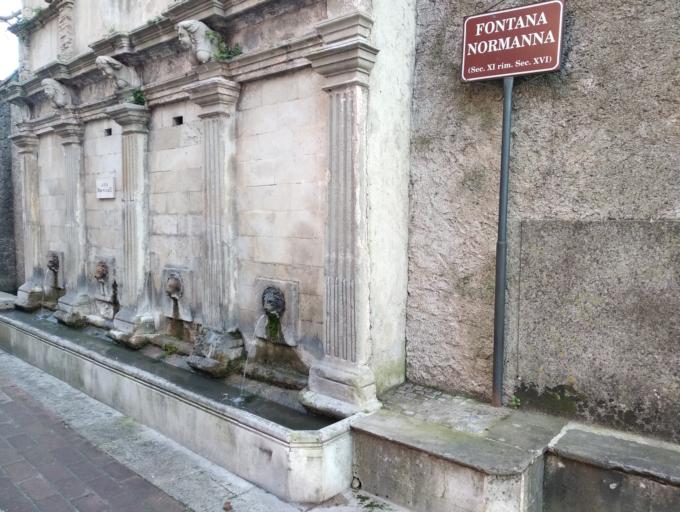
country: IT
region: Calabria
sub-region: Provincia di Cosenza
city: San Marco Argentano
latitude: 39.5563
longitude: 16.1189
